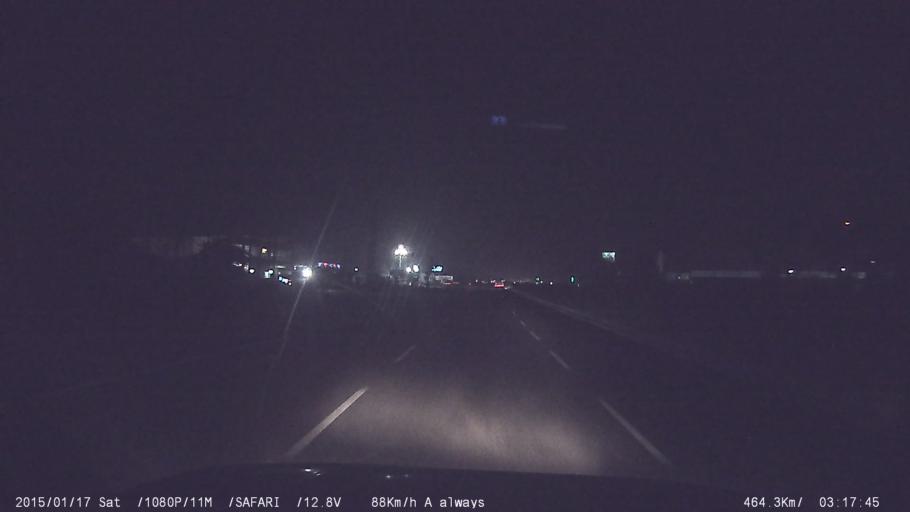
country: IN
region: Tamil Nadu
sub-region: Krishnagiri
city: Kelamangalam
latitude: 12.6802
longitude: 77.9544
